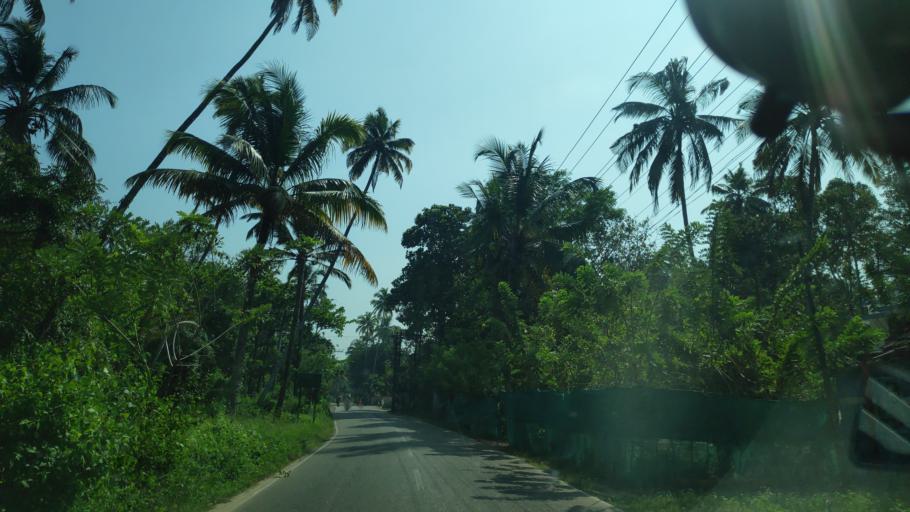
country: IN
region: Kerala
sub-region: Alappuzha
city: Vayalar
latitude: 9.6426
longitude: 76.2985
